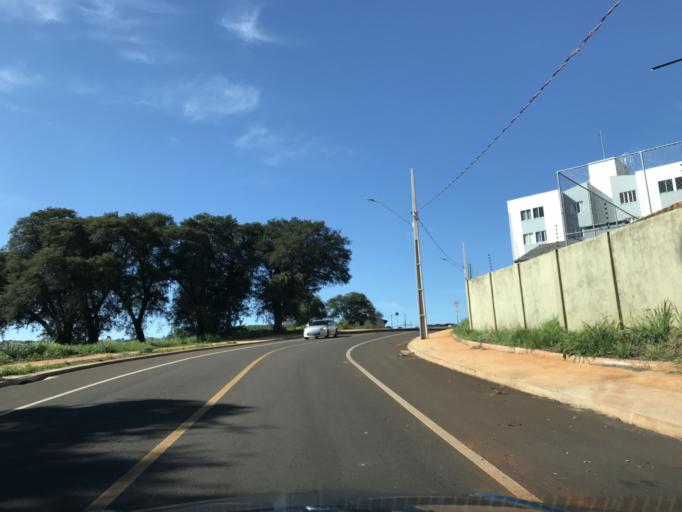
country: BR
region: Parana
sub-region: Cascavel
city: Cascavel
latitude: -24.9358
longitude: -53.4724
